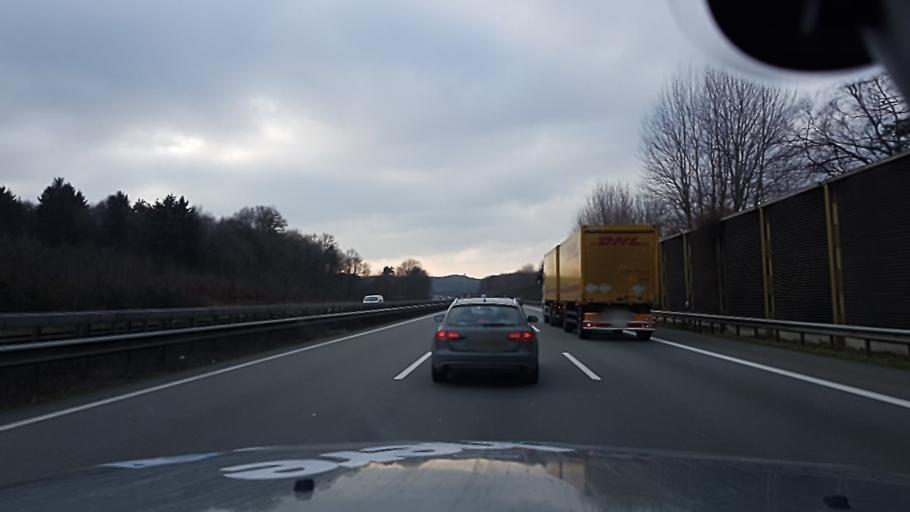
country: DE
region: Lower Saxony
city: Wallenhorst
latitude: 52.3274
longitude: 7.9760
